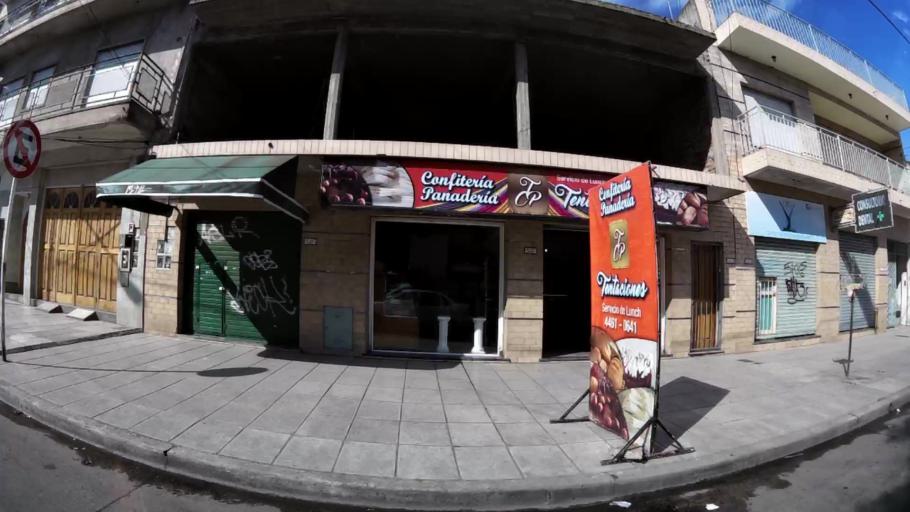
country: AR
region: Buenos Aires
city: San Justo
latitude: -34.6697
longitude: -58.5722
